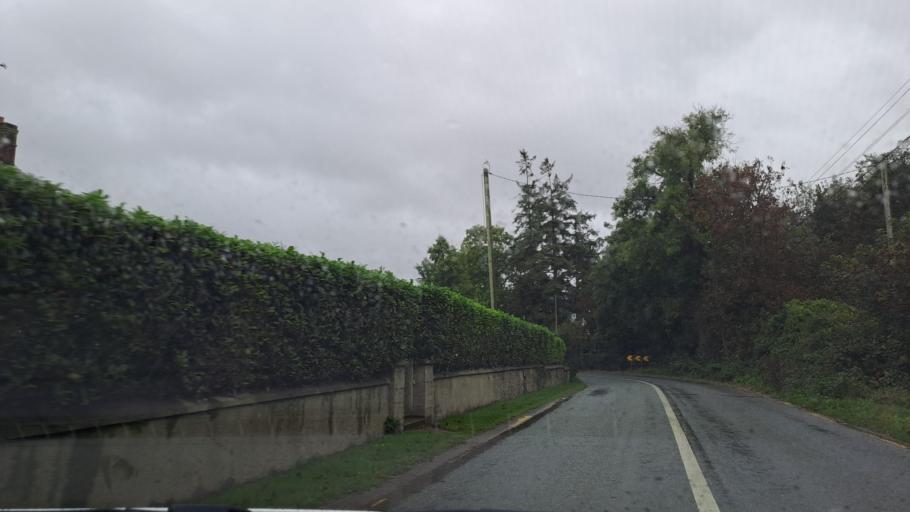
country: IE
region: Leinster
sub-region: Lu
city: Dundalk
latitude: 53.9663
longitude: -6.4738
